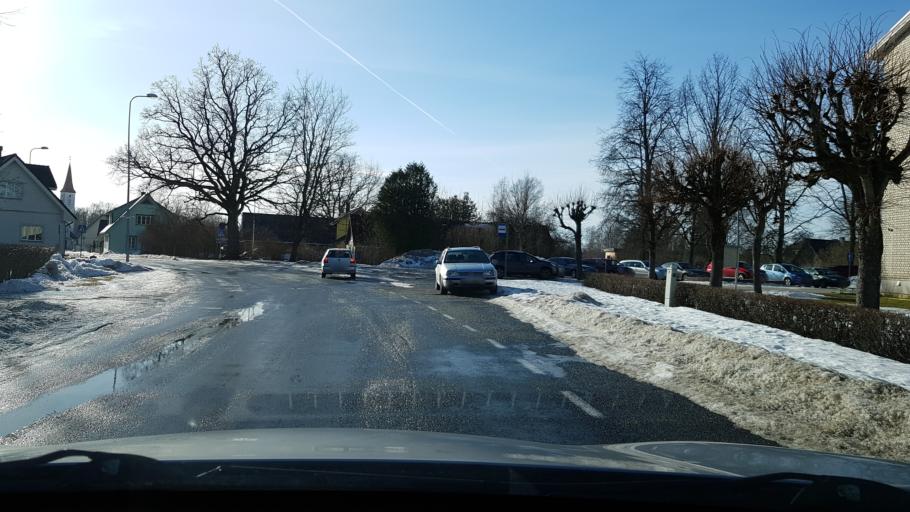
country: EE
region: Viljandimaa
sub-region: Suure-Jaani vald
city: Suure-Jaani
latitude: 58.5381
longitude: 25.4701
